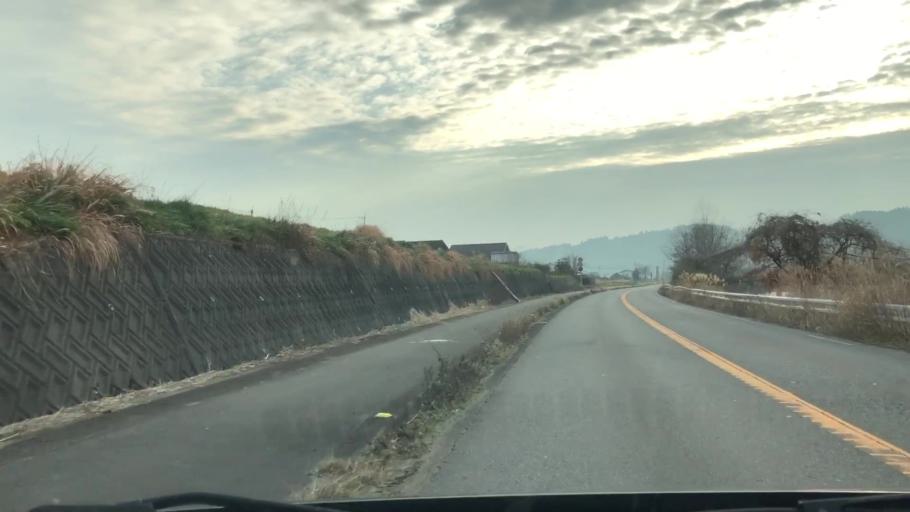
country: JP
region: Oita
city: Takedamachi
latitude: 32.9679
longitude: 131.4775
